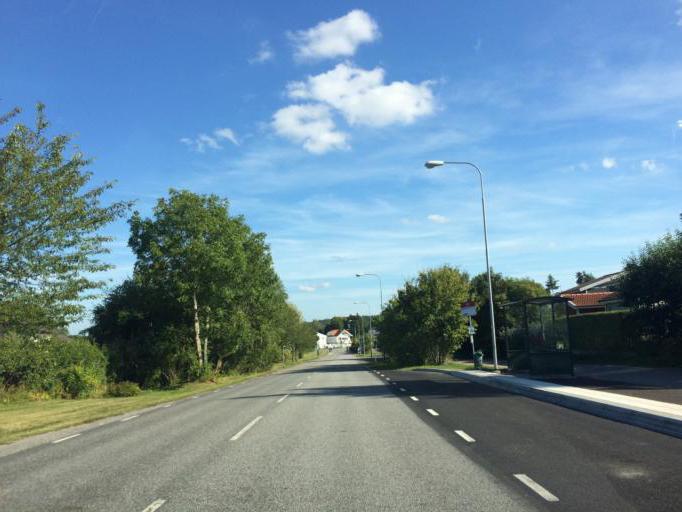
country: SE
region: Stockholm
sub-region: Upplands Vasby Kommun
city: Upplands Vaesby
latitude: 59.4937
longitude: 17.9435
